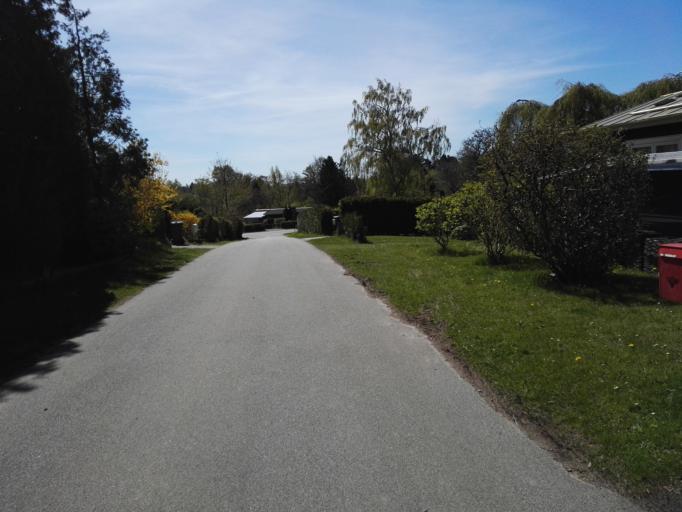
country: DK
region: Capital Region
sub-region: Frederikssund Kommune
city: Frederikssund
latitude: 55.9025
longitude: 12.0551
